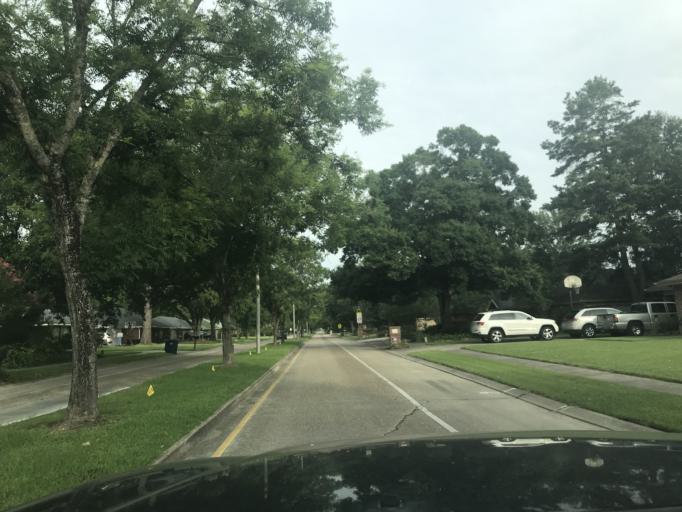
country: US
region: Louisiana
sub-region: Lafayette Parish
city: Lafayette
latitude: 30.1963
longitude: -92.0473
